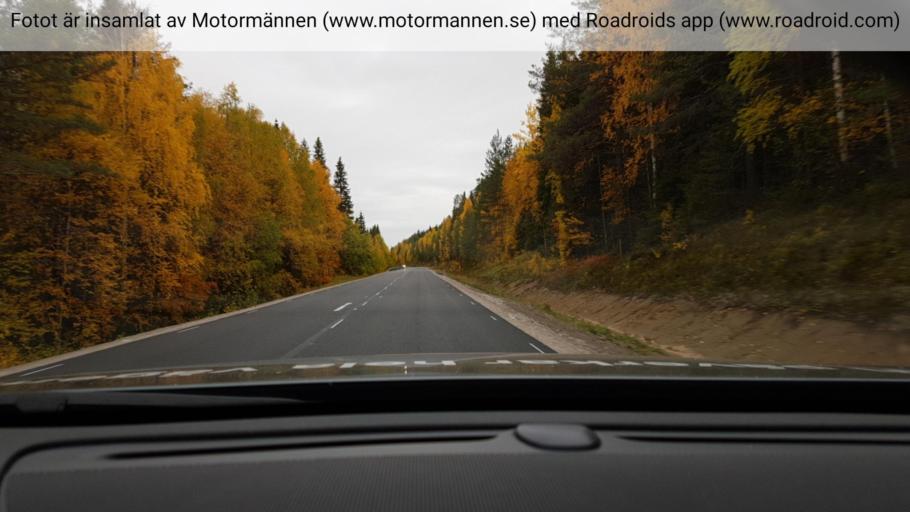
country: SE
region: Norrbotten
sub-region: Overkalix Kommun
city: OEverkalix
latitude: 66.4718
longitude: 22.7914
